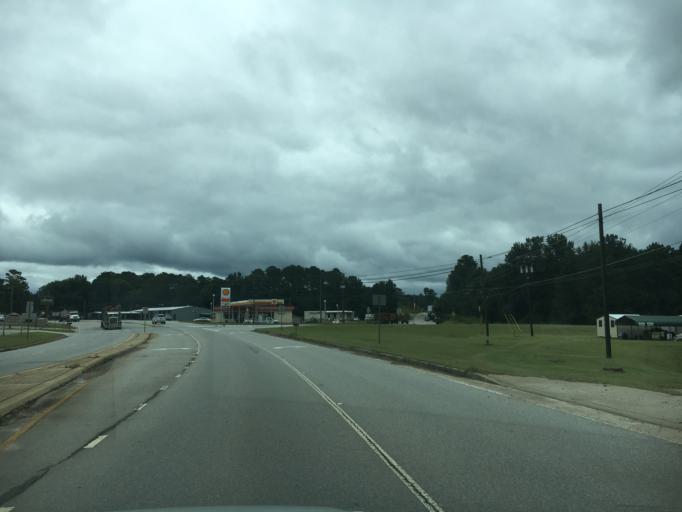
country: US
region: Georgia
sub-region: Wilkes County
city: Washington
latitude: 33.7255
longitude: -82.7135
